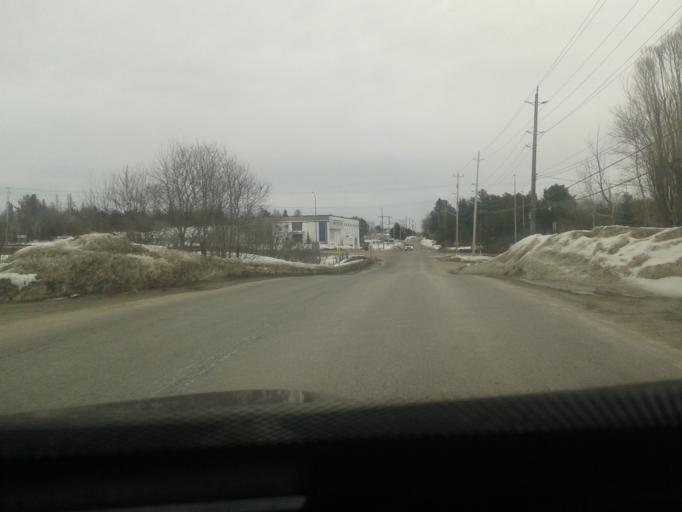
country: CA
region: Ontario
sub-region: Nipissing District
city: North Bay
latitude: 46.3471
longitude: -79.4728
